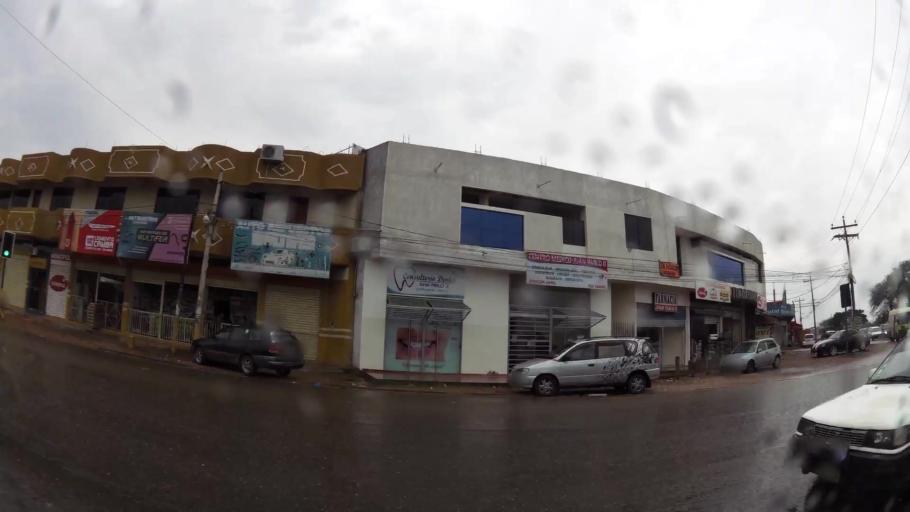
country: BO
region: Santa Cruz
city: Santa Cruz de la Sierra
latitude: -17.7990
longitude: -63.1498
